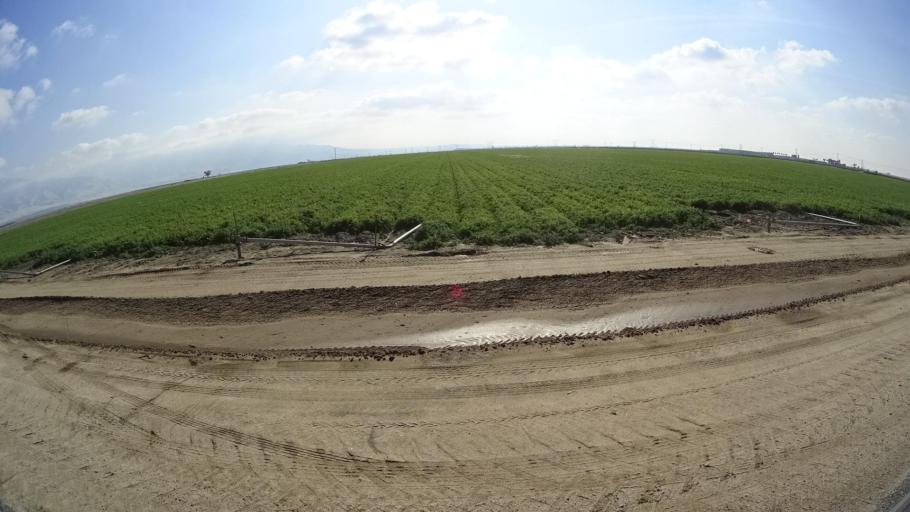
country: US
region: California
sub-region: Kern County
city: Arvin
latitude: 35.2674
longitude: -118.8217
